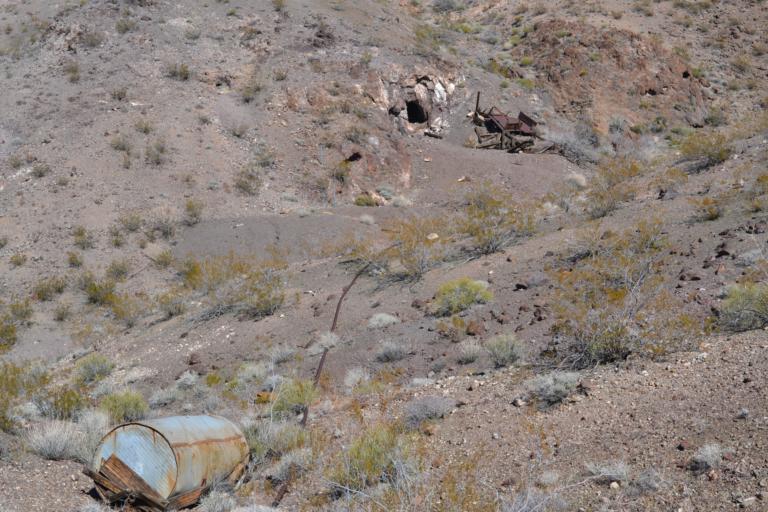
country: US
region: Nevada
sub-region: Clark County
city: Boulder City
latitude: 36.0112
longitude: -114.6770
